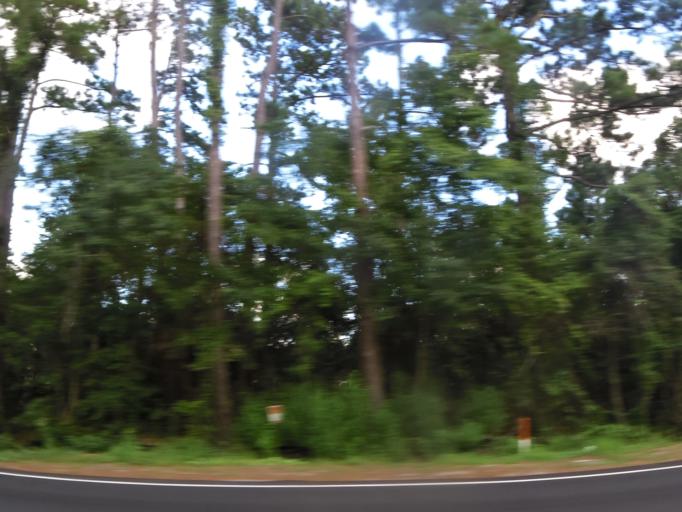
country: US
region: Georgia
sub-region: Glynn County
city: Saint Simon Mills
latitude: 31.1683
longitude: -81.4045
